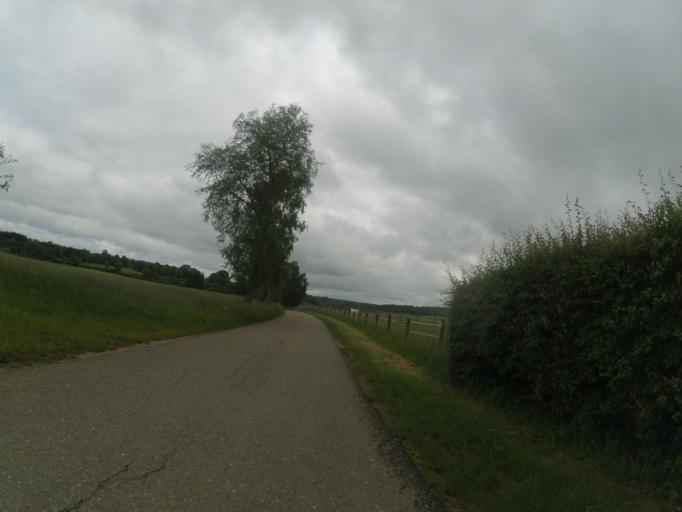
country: DE
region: Baden-Wuerttemberg
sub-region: Tuebingen Region
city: Bernstadt
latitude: 48.5060
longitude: 10.0241
